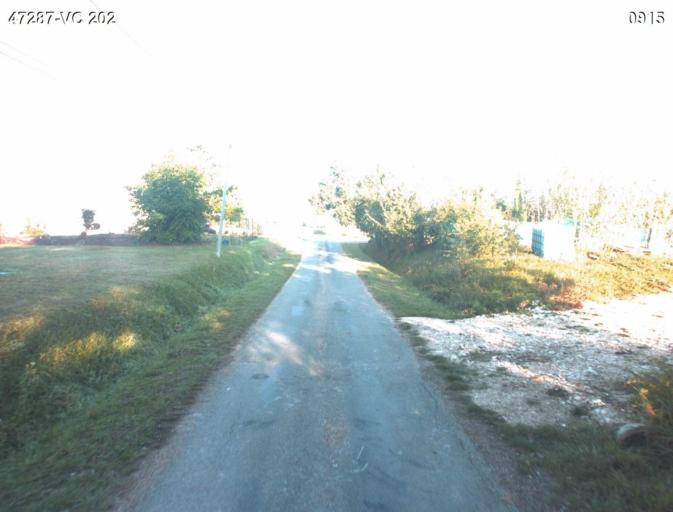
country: FR
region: Aquitaine
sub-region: Departement du Lot-et-Garonne
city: Laplume
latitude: 44.1173
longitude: 0.4613
